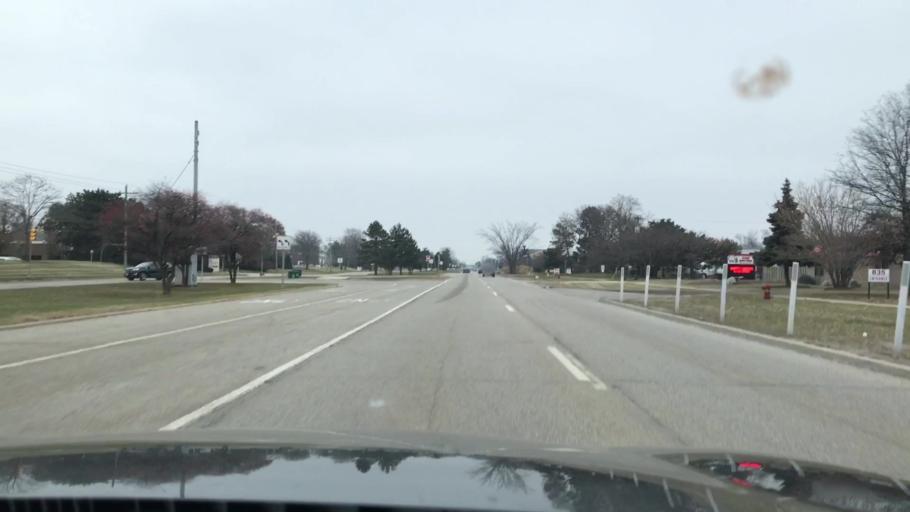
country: US
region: Michigan
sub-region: Oakland County
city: Clawson
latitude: 42.5421
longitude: -83.1205
